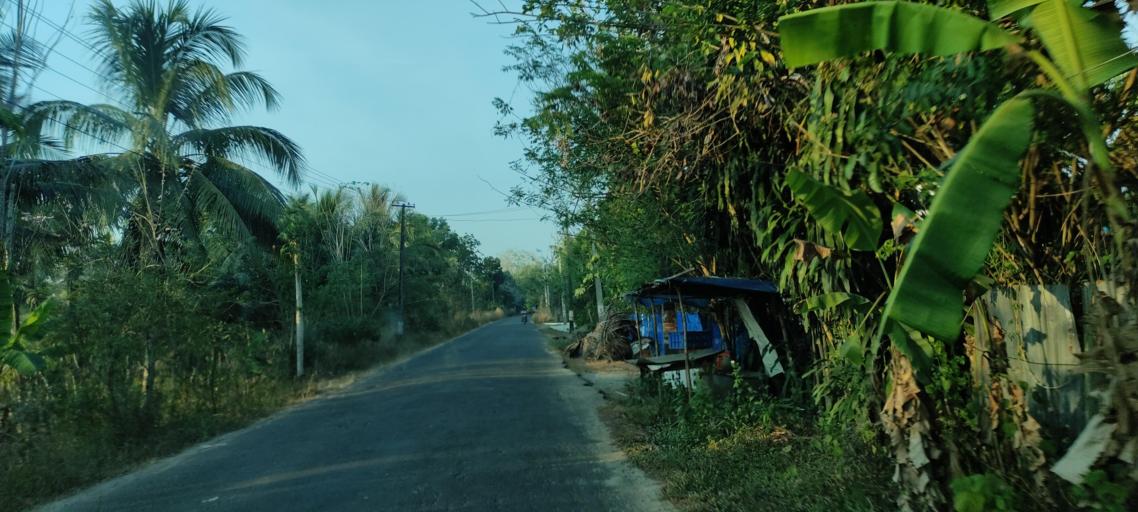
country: IN
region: Kerala
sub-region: Alappuzha
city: Kutiatodu
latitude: 9.7648
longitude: 76.3533
